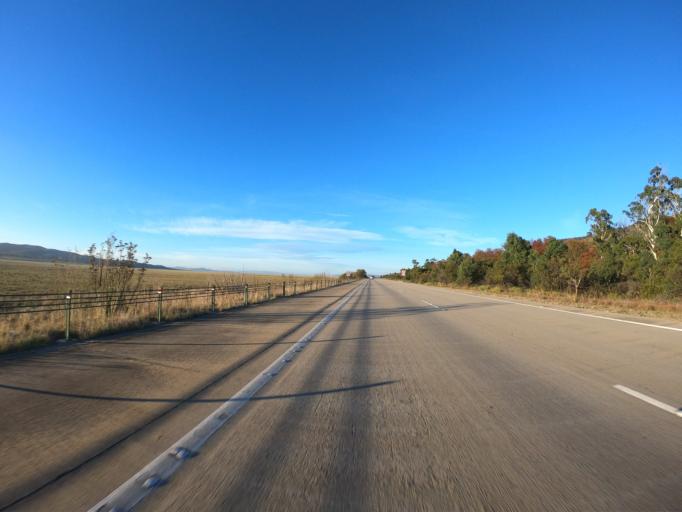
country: AU
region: New South Wales
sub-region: Yass Valley
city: Gundaroo
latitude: -34.9848
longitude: 149.3876
